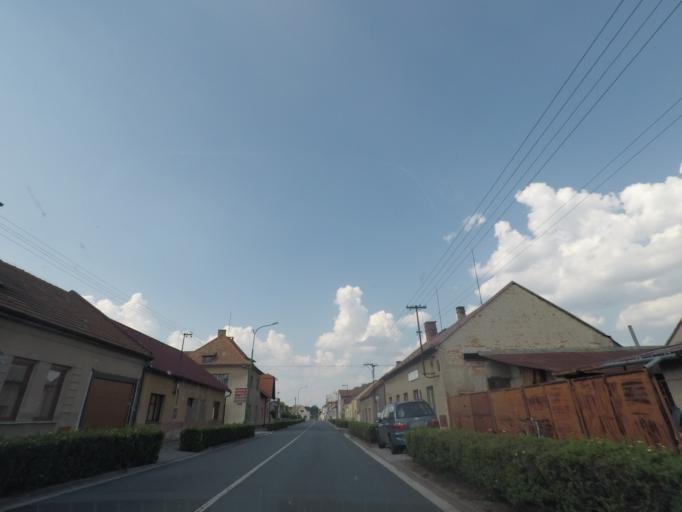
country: CZ
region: Pardubicky
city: Horni Jeleni
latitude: 50.0471
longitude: 16.0825
